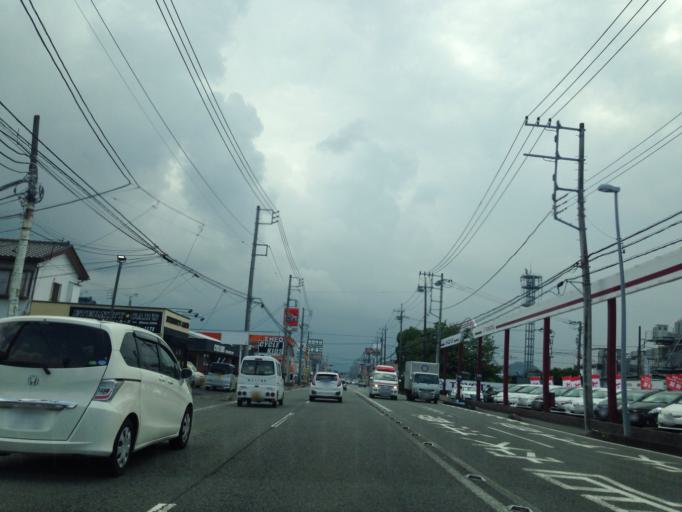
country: JP
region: Shizuoka
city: Mishima
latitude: 35.0901
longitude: 138.9289
